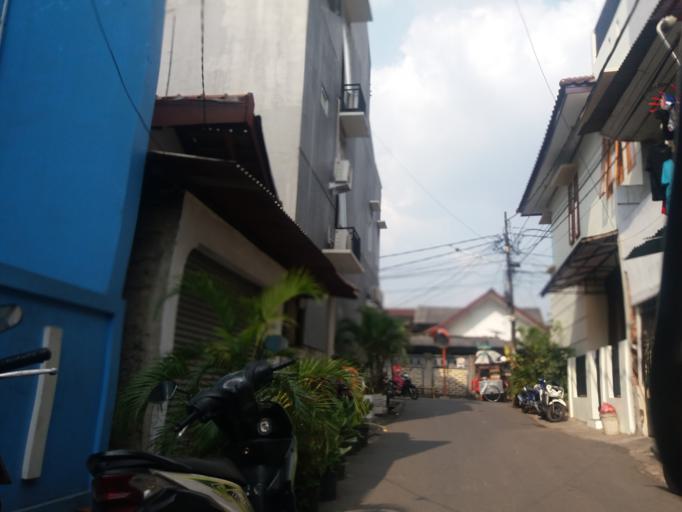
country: ID
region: Jakarta Raya
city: Jakarta
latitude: -6.2180
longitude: 106.8247
